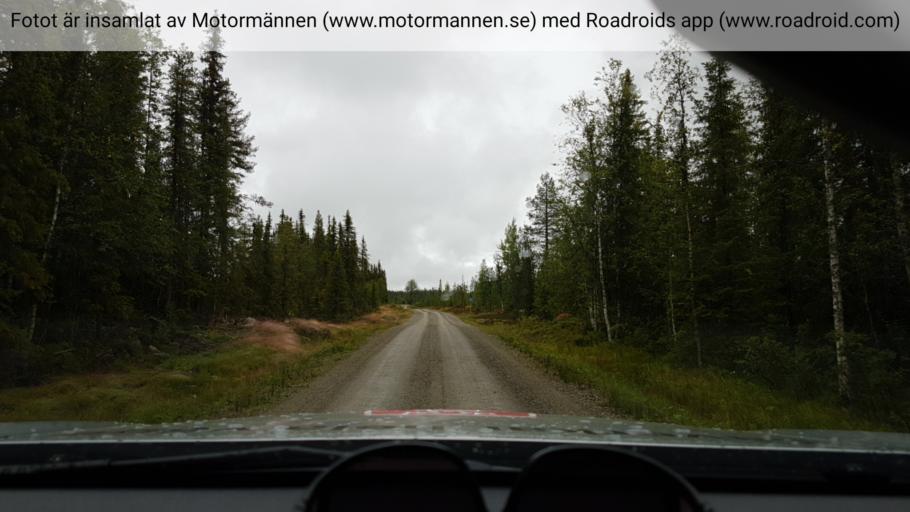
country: SE
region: Vaesterbotten
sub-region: Storumans Kommun
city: Storuman
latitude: 64.8408
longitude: 17.4048
